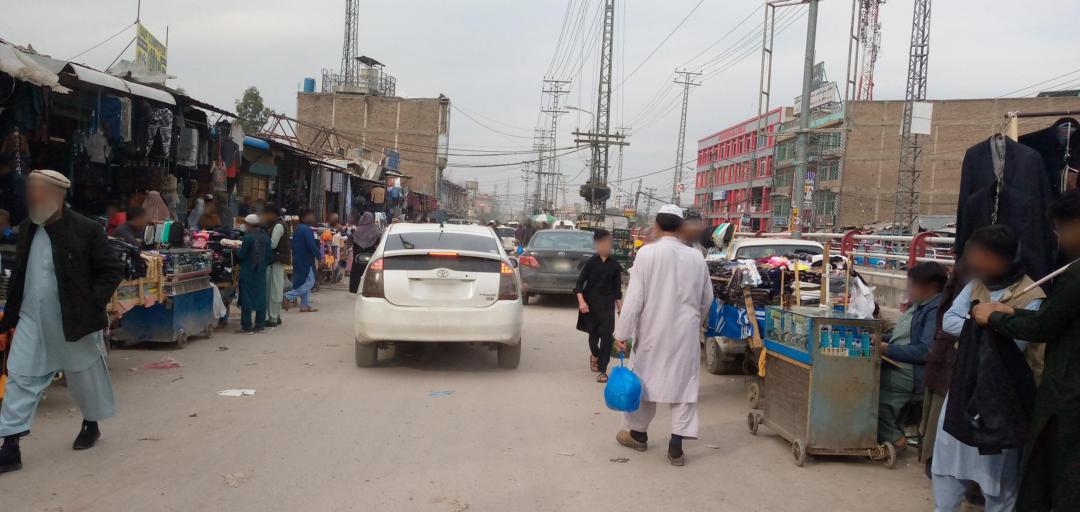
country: PK
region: Khyber Pakhtunkhwa
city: Peshawar
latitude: 33.9960
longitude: 71.4699
